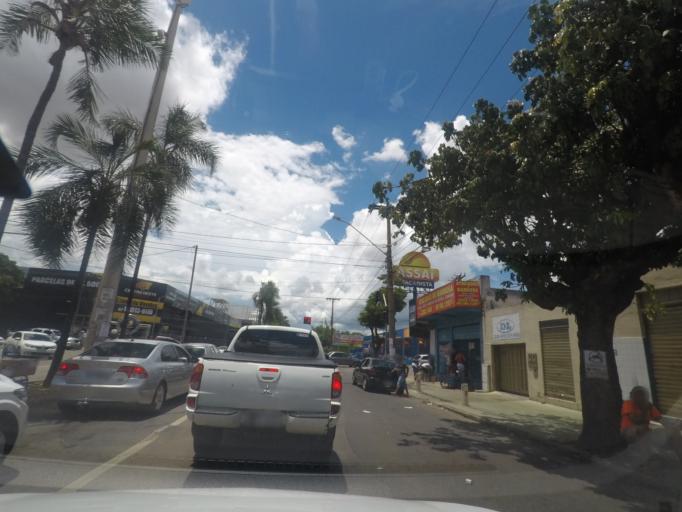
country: BR
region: Goias
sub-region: Goiania
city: Goiania
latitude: -16.6631
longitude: -49.2570
